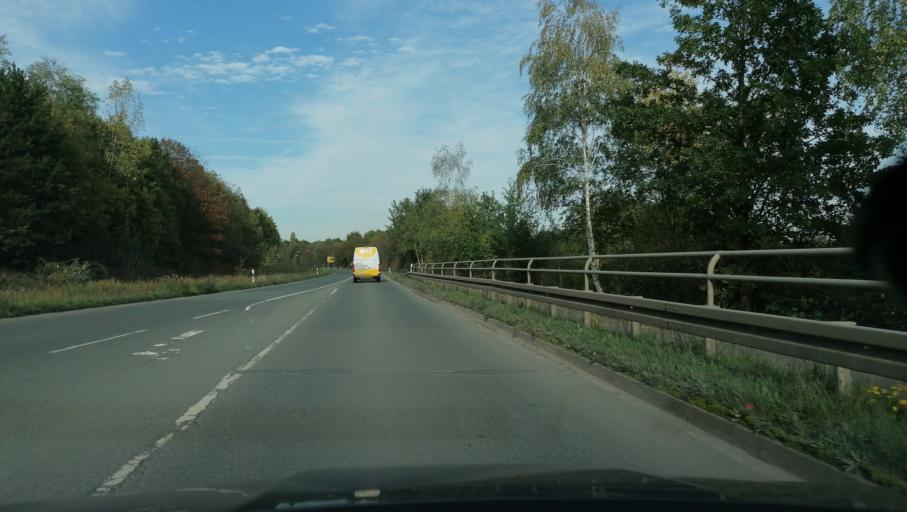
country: DE
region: North Rhine-Westphalia
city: Herten
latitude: 51.5658
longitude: 7.1750
